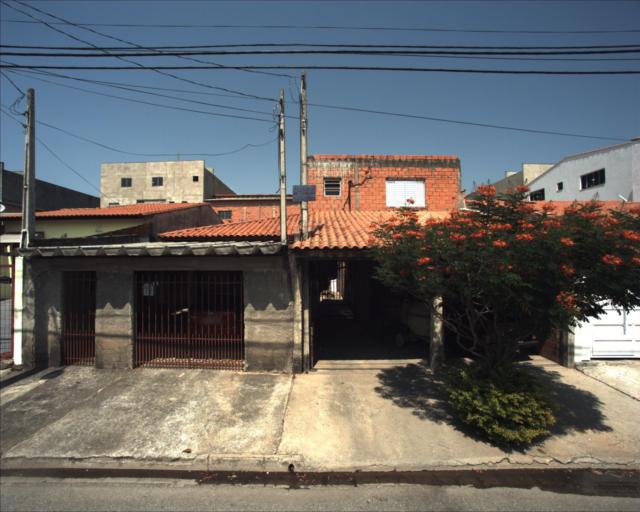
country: BR
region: Sao Paulo
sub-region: Sorocaba
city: Sorocaba
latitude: -23.4354
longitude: -47.4815
